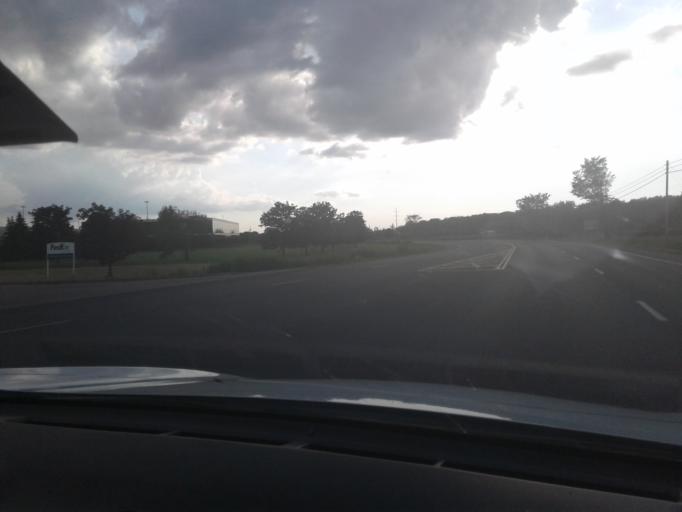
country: US
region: New York
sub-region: Onondaga County
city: East Syracuse
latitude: 43.0935
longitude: -76.0615
